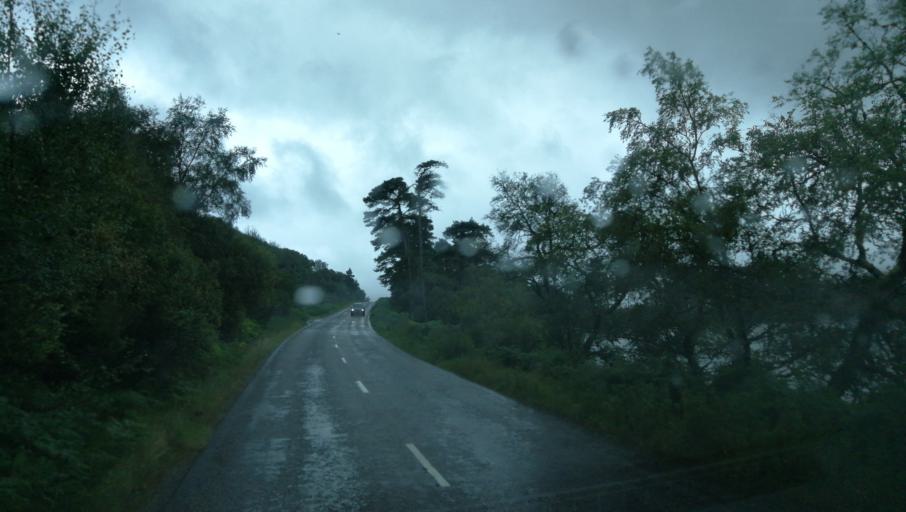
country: GB
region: Scotland
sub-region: Highland
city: Ullapool
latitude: 57.9885
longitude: -5.1138
